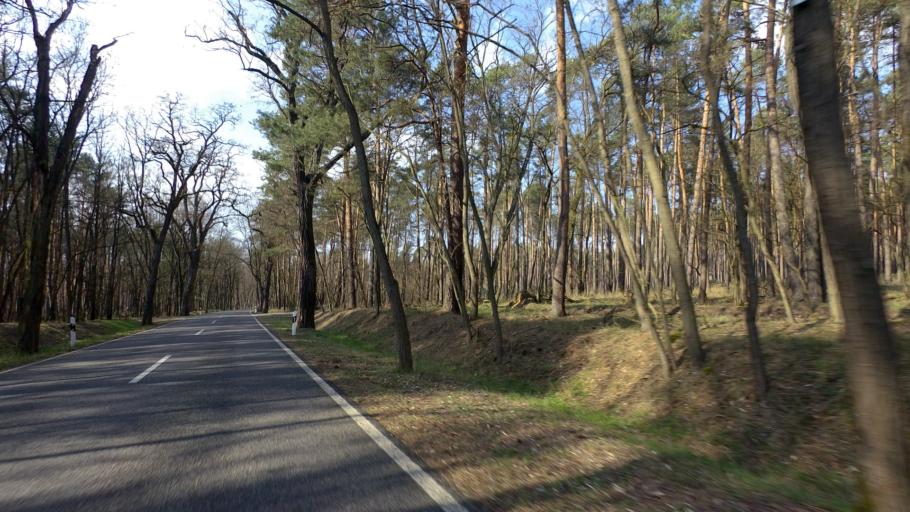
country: DE
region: Brandenburg
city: Dahme
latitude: 51.9294
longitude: 13.4571
